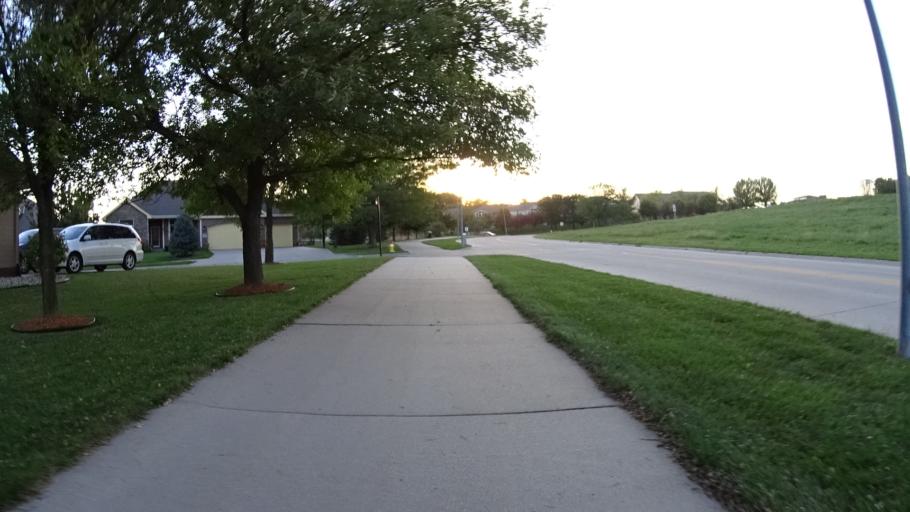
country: US
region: Nebraska
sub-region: Sarpy County
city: Papillion
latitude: 41.1381
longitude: -95.9842
